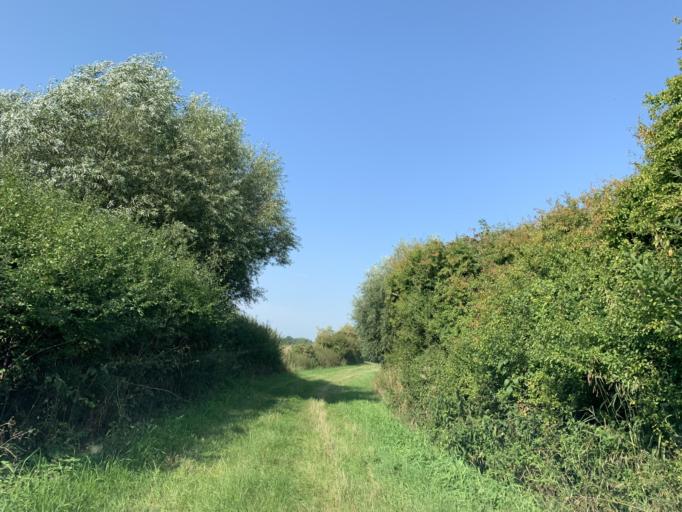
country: DE
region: Mecklenburg-Vorpommern
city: Blankensee
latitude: 53.3940
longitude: 13.2477
